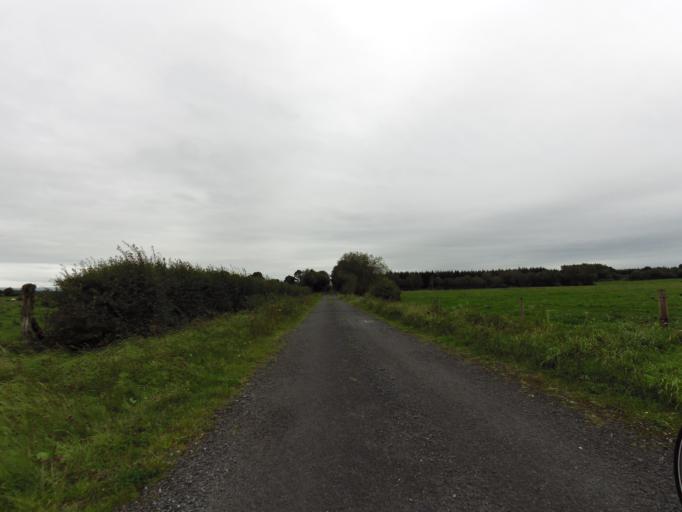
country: IE
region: Leinster
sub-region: Uibh Fhaili
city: Ferbane
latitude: 53.2495
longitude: -7.7382
